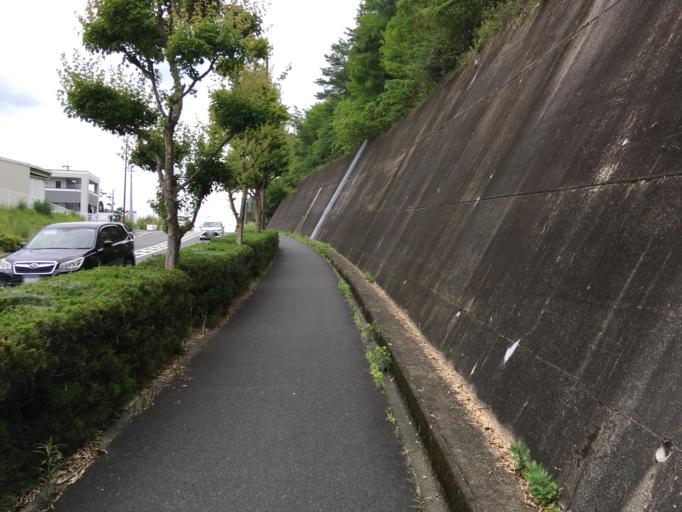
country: JP
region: Nara
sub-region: Ikoma-shi
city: Ikoma
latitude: 34.7226
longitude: 135.7080
